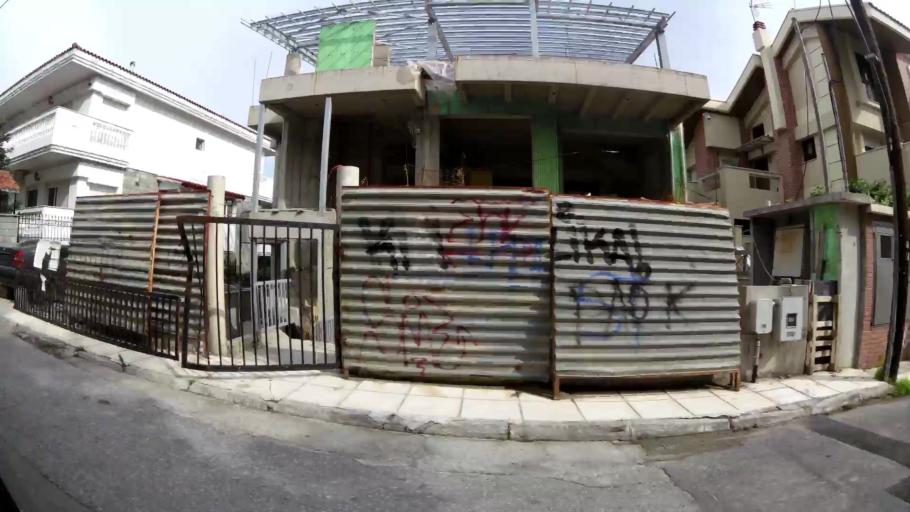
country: GR
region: Central Macedonia
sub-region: Nomos Thessalonikis
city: Panorama
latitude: 40.5897
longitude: 23.0307
